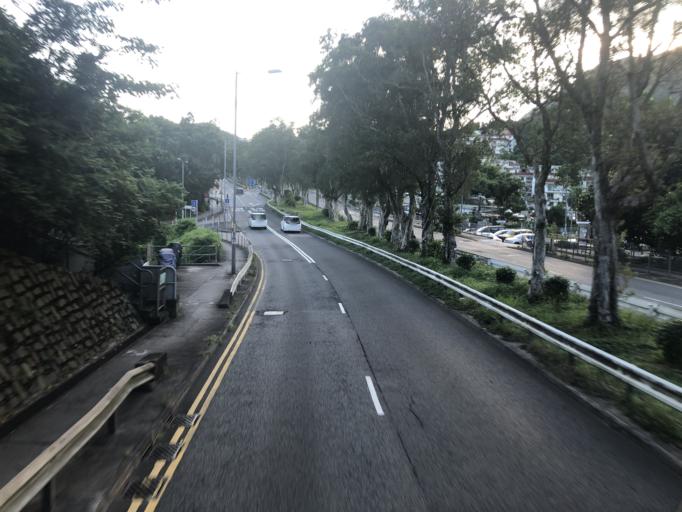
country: HK
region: Sai Kung
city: Sai Kung
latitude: 22.3345
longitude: 114.2393
